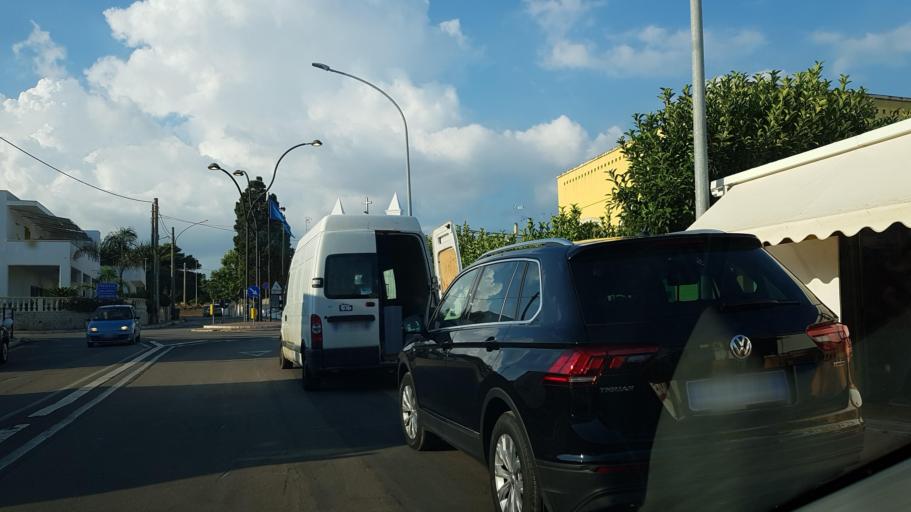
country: IT
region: Apulia
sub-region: Provincia di Lecce
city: Gemini
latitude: 39.8439
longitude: 18.2100
